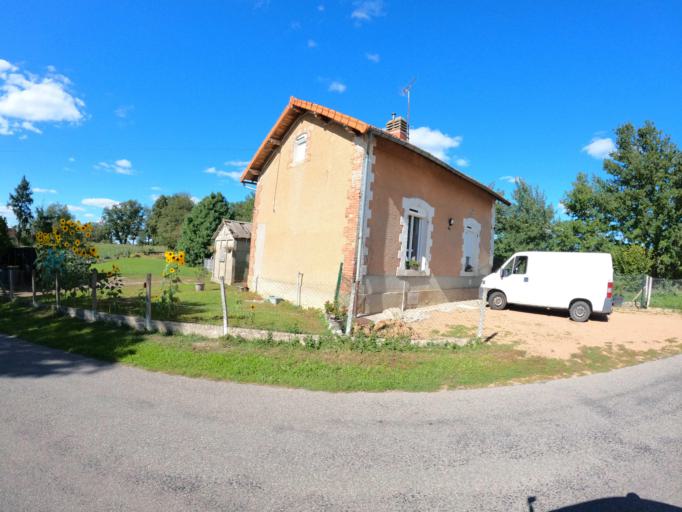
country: FR
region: Auvergne
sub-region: Departement de l'Allier
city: Doyet
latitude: 46.3976
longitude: 2.8745
